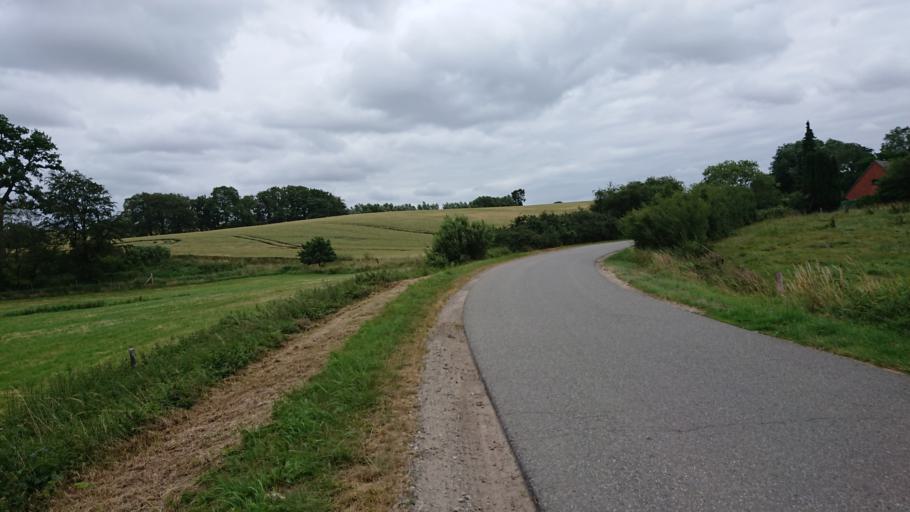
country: DE
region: Schleswig-Holstein
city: Gross Sarau
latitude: 53.7845
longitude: 10.7287
